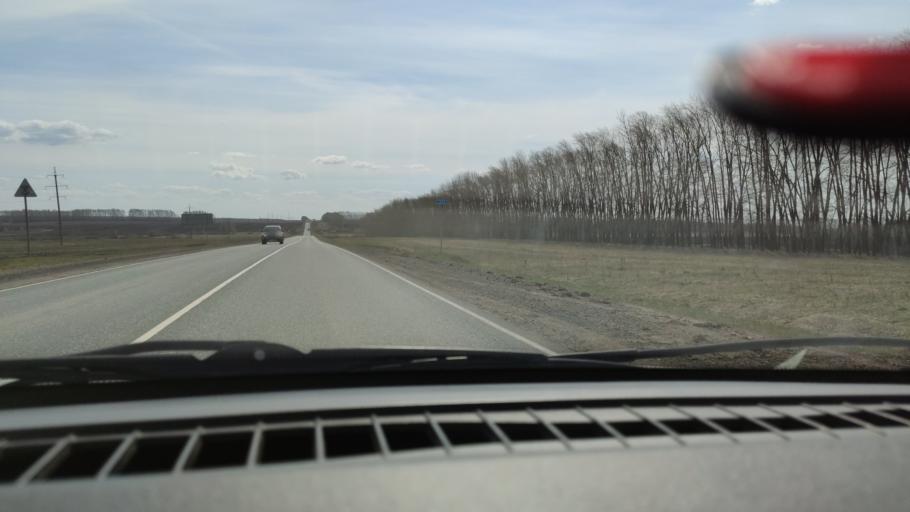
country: RU
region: Bashkortostan
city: Dyurtyuli
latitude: 55.2586
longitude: 55.0624
